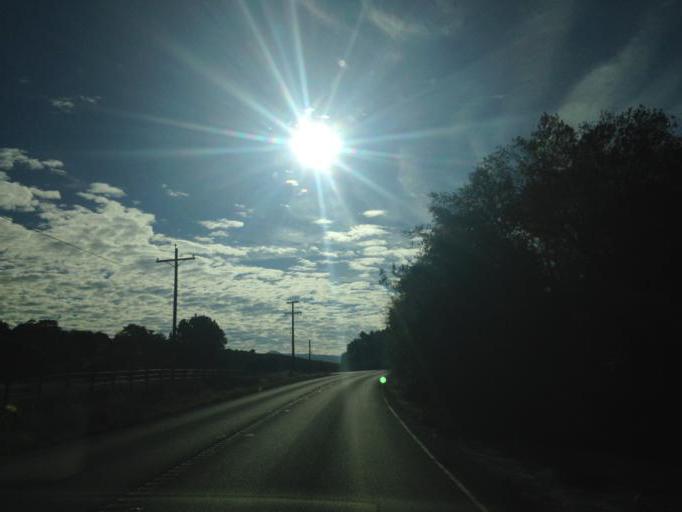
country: US
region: California
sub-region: San Diego County
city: Ramona
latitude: 33.2368
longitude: -116.7627
